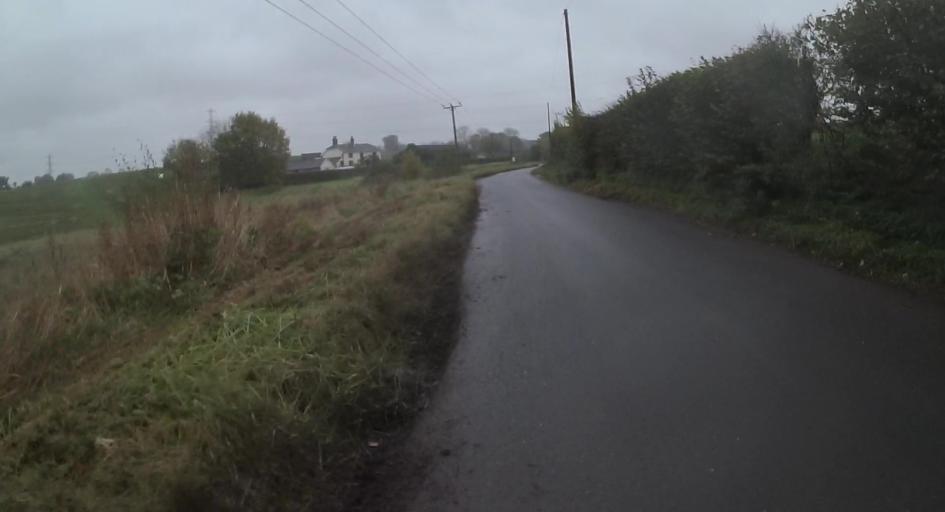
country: GB
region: England
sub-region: Hampshire
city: Kingsley
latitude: 51.1640
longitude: -0.9222
